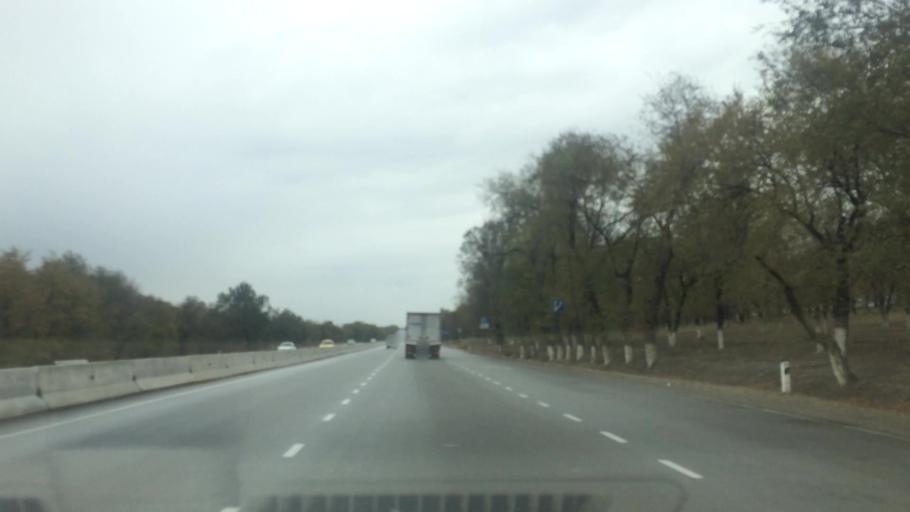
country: UZ
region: Samarqand
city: Bulung'ur
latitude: 39.9024
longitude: 67.5025
